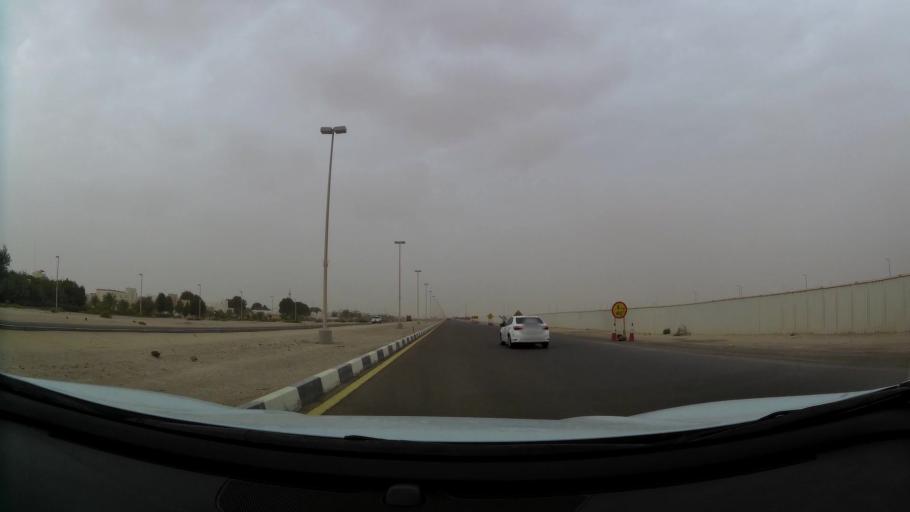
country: AE
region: Abu Dhabi
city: Abu Dhabi
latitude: 24.4274
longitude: 54.7239
